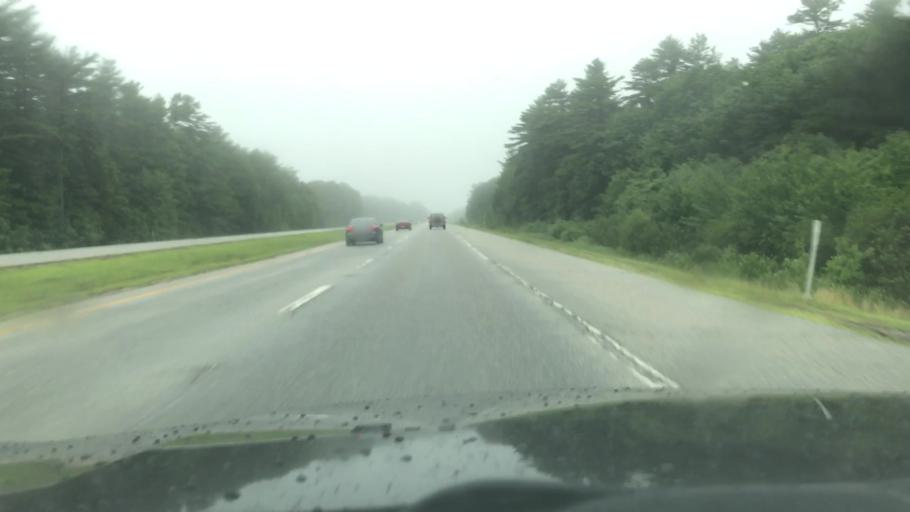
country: US
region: Maine
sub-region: Cumberland County
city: South Portland Gardens
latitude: 43.6126
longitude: -70.3204
